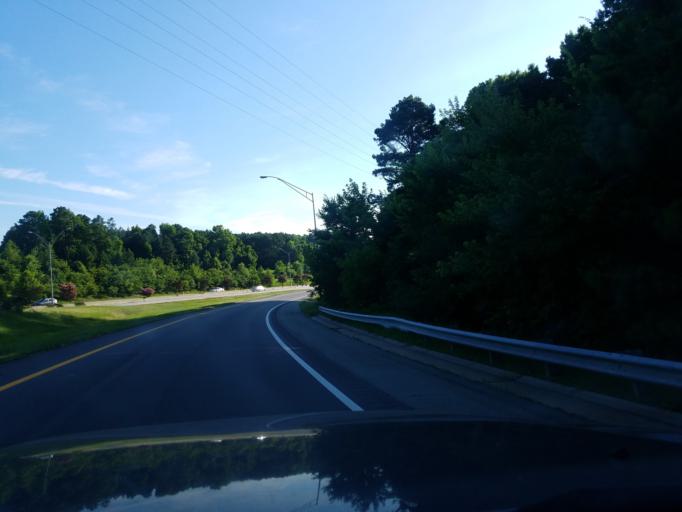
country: US
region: North Carolina
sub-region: Durham County
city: Durham
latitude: 36.0136
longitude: -78.8686
